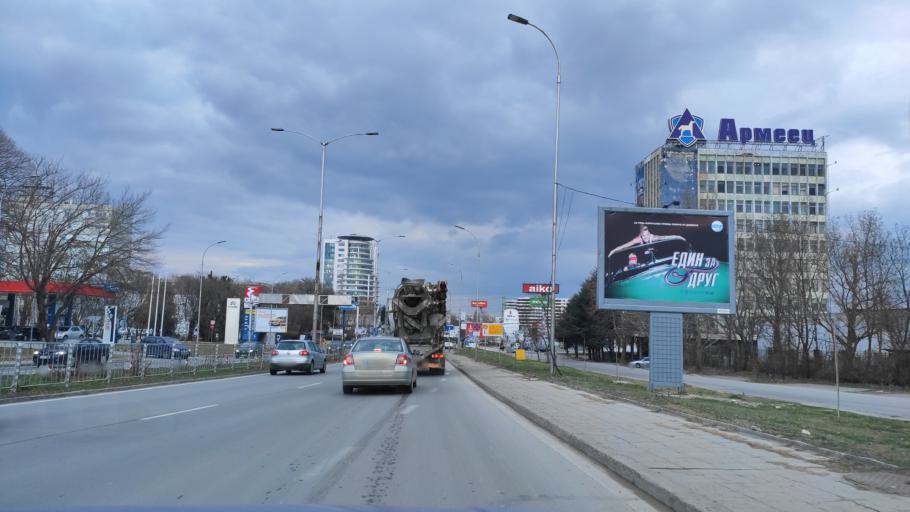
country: BG
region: Varna
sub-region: Obshtina Varna
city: Varna
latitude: 43.2226
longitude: 27.8700
